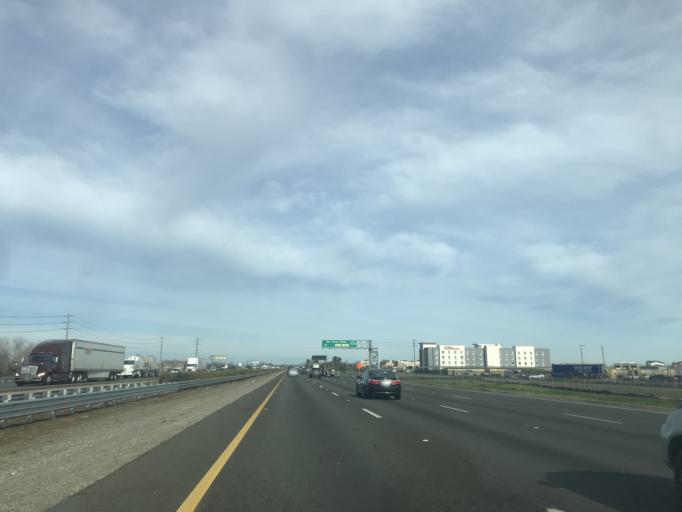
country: US
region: California
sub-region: Yolo County
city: West Sacramento
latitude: 38.6469
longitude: -121.5281
